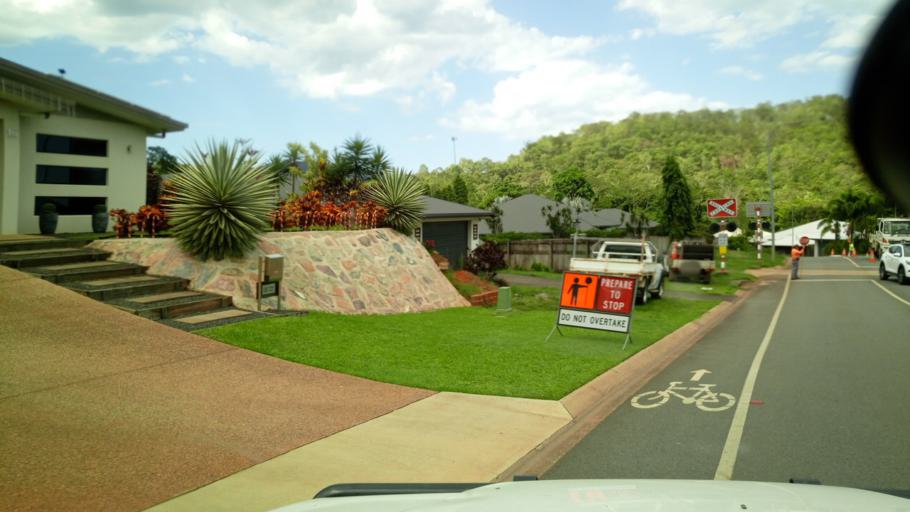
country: AU
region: Queensland
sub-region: Cairns
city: Woree
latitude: -16.9203
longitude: 145.7214
